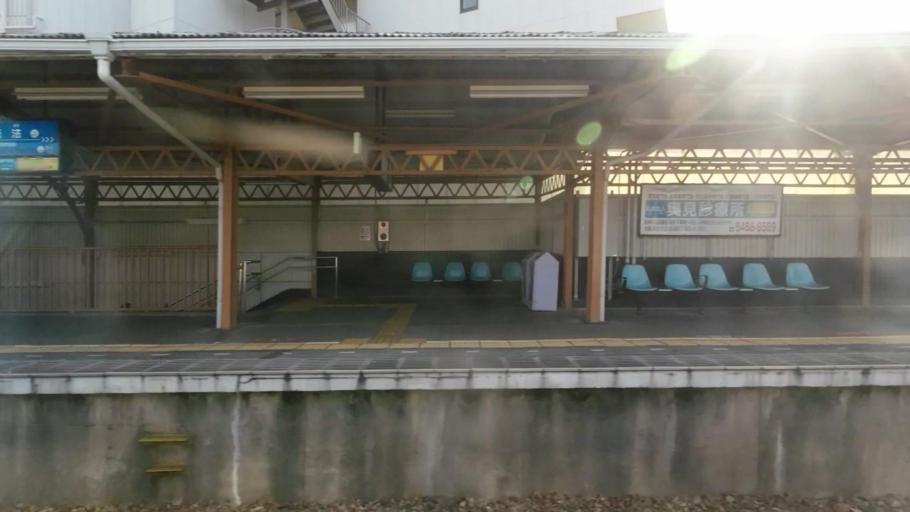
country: JP
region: Hyogo
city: Amagasaki
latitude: 34.6890
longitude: 135.4519
